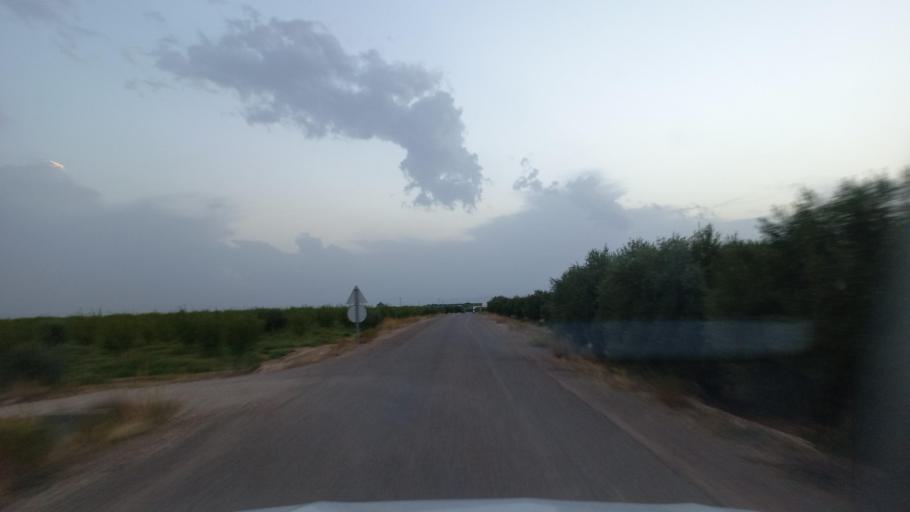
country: TN
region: Al Qasrayn
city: Kasserine
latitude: 35.2745
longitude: 9.0420
